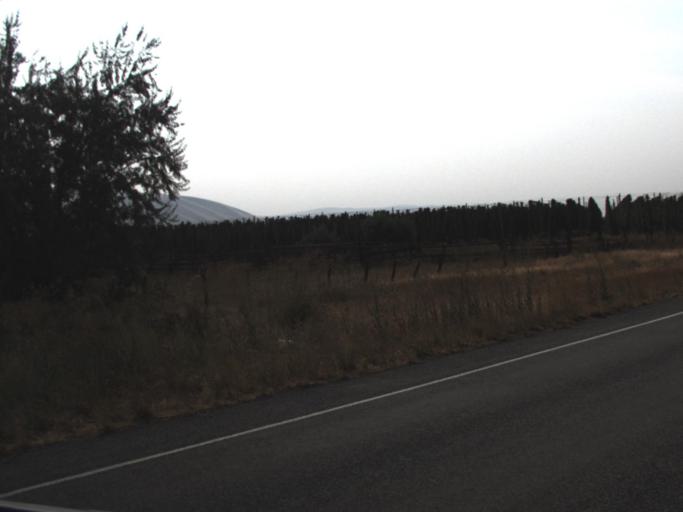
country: US
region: Washington
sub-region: Yakima County
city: Granger
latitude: 46.3241
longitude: -120.2350
